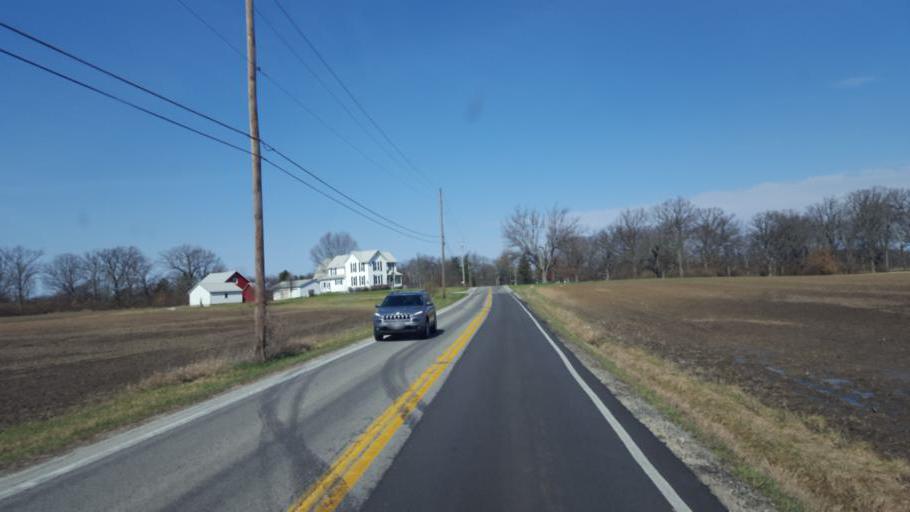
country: US
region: Ohio
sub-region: Marion County
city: Marion
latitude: 40.5688
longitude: -83.0894
